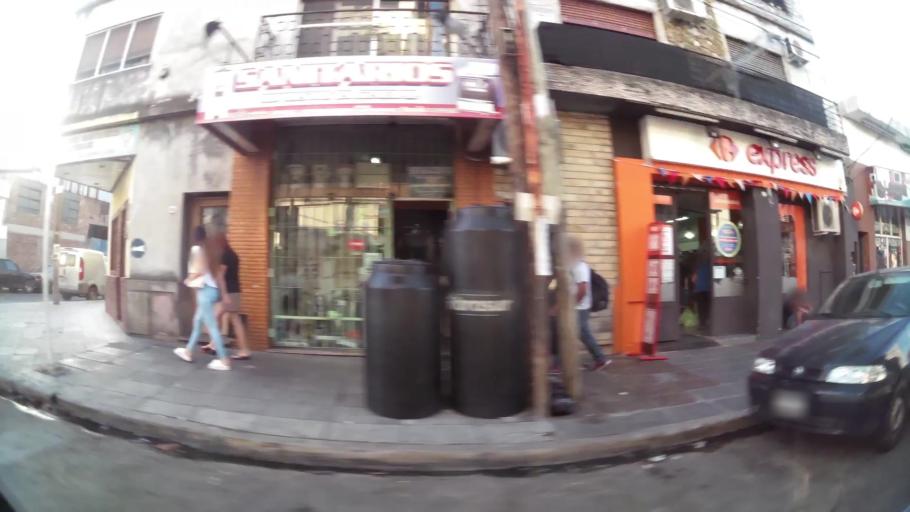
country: AR
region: Buenos Aires F.D.
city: Villa Lugano
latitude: -34.6912
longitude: -58.4817
